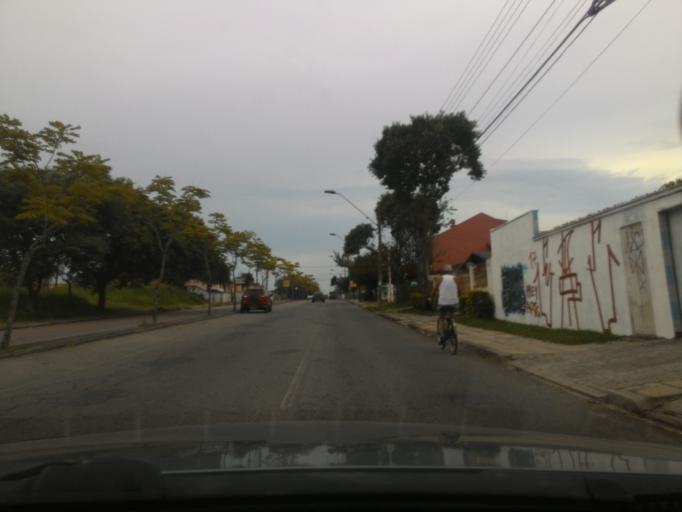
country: BR
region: Parana
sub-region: Pinhais
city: Pinhais
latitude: -25.4423
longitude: -49.2163
